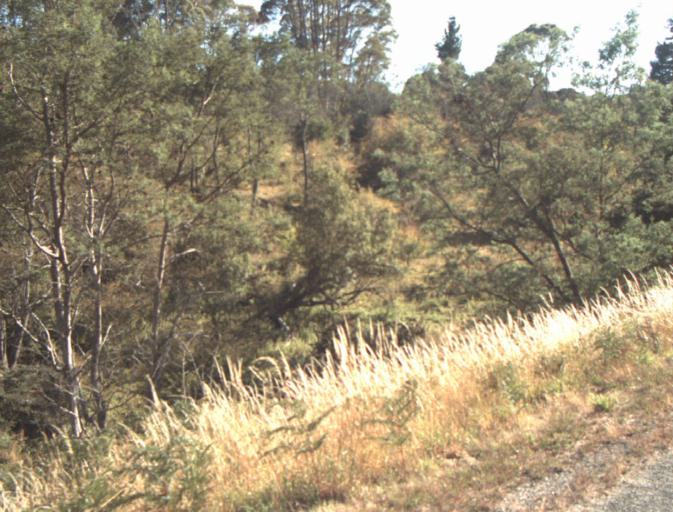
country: AU
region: Tasmania
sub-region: Launceston
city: Newstead
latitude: -41.4191
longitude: 147.2770
